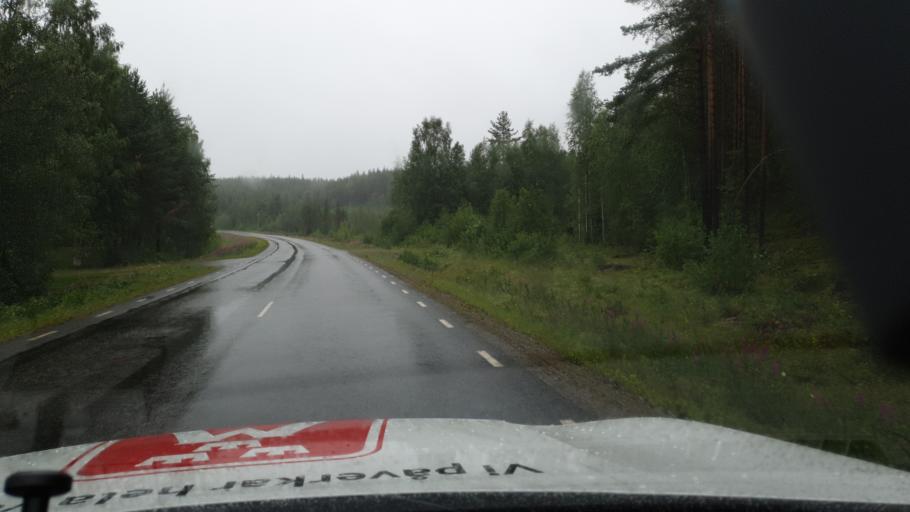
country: SE
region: Vaesterbotten
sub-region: Norsjo Kommun
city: Norsjoe
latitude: 64.8502
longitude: 19.7493
